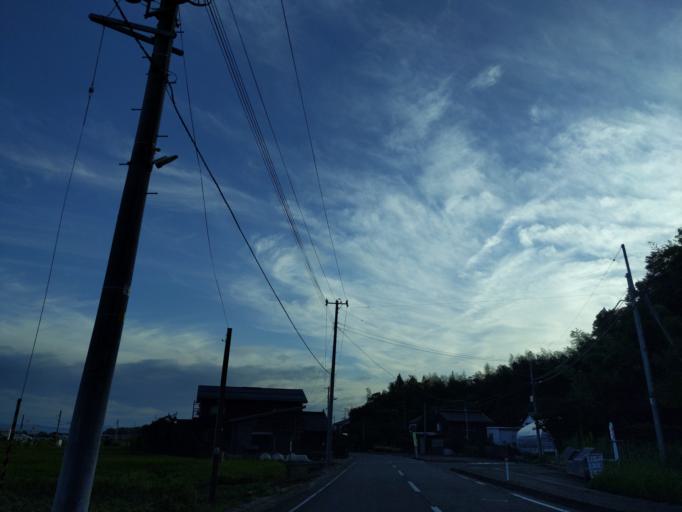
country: JP
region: Niigata
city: Kashiwazaki
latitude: 37.4349
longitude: 138.6236
